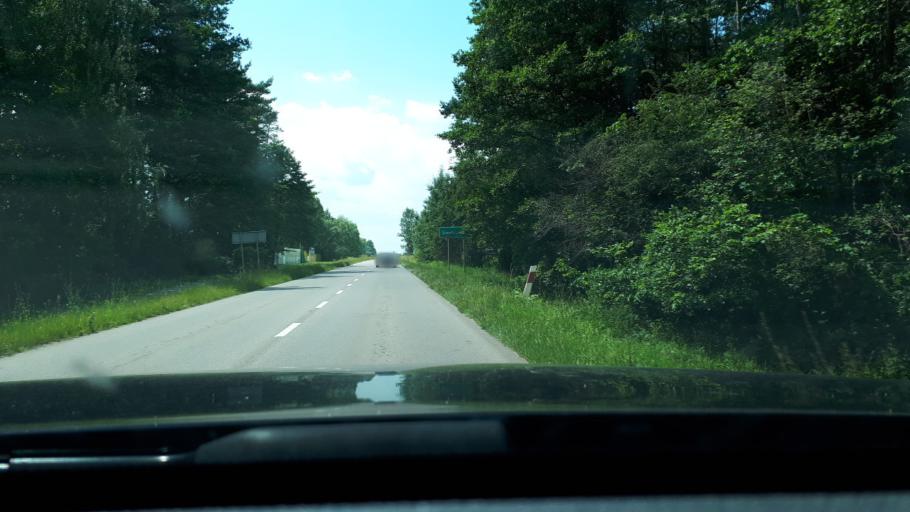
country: PL
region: Podlasie
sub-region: Powiat bialostocki
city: Choroszcz
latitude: 53.1309
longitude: 23.0366
